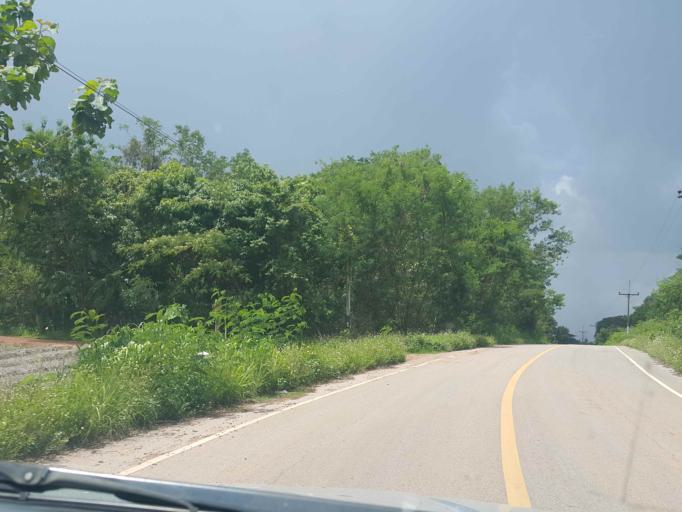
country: TH
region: Phayao
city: Dok Kham Tai
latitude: 19.0498
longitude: 99.9506
